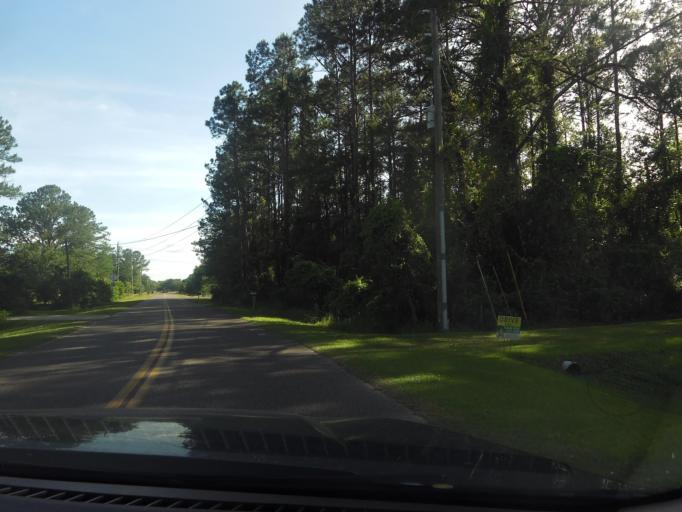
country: US
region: Florida
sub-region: Nassau County
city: Nassau Village-Ratliff
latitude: 30.5256
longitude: -81.7766
